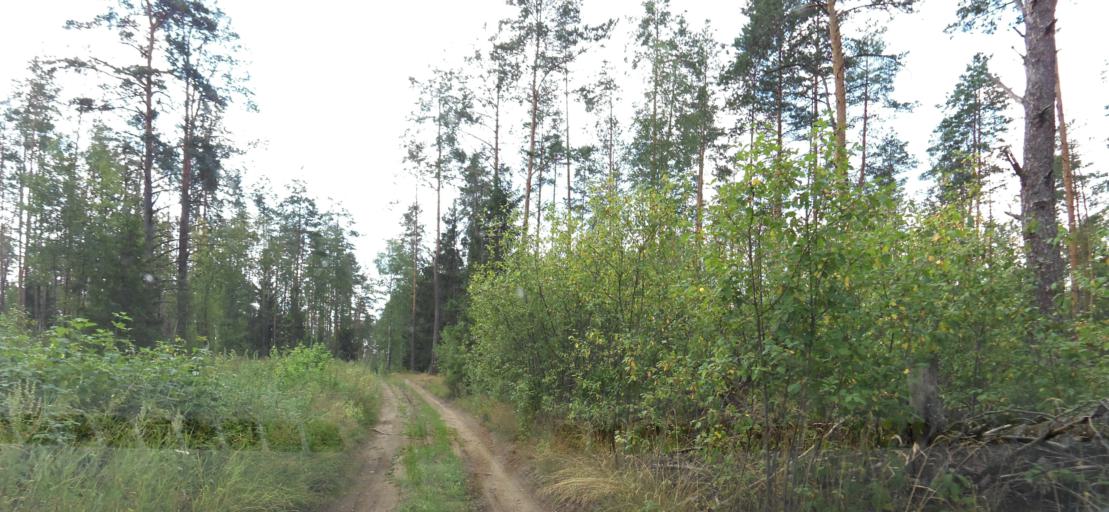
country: LT
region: Alytaus apskritis
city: Varena
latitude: 54.2428
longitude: 24.6545
